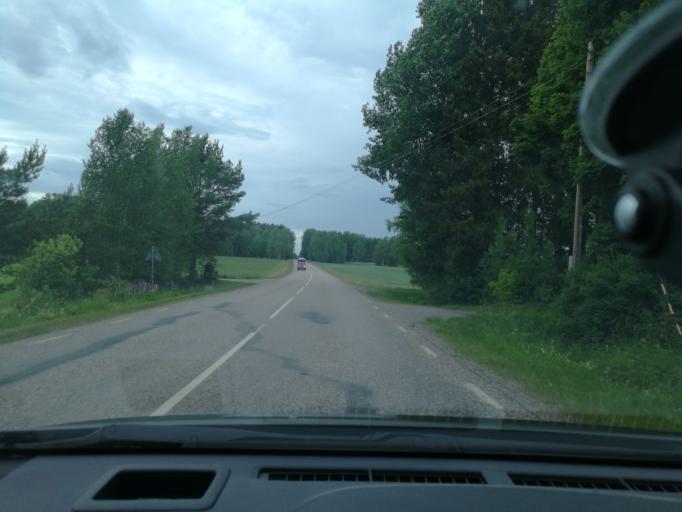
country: SE
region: Vaestmanland
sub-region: Vasteras
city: Skultuna
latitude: 59.8887
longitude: 16.3669
